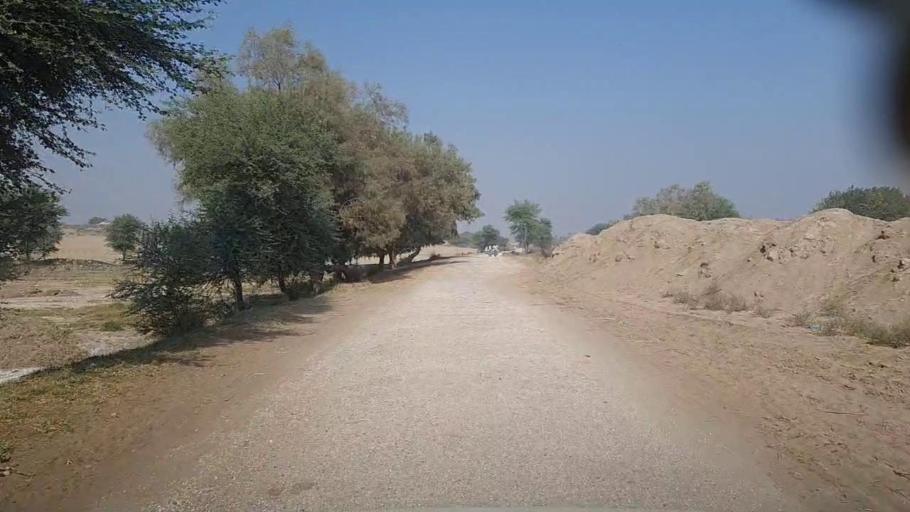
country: PK
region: Sindh
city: Kandiari
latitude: 26.9225
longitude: 68.5178
